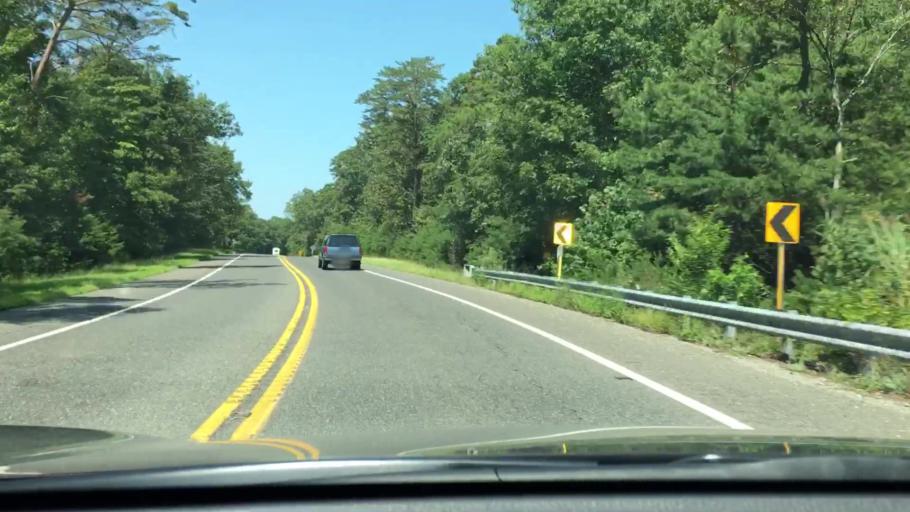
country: US
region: New Jersey
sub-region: Cumberland County
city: Port Norris
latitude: 39.2850
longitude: -74.9528
